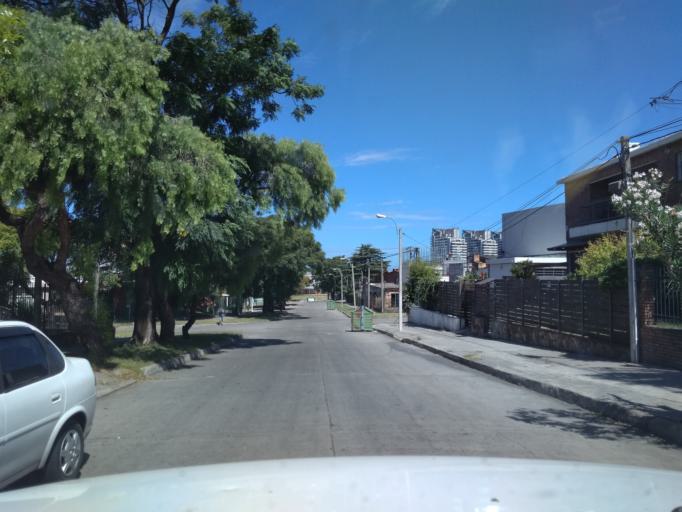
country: UY
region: Montevideo
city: Montevideo
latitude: -34.8900
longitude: -56.1202
